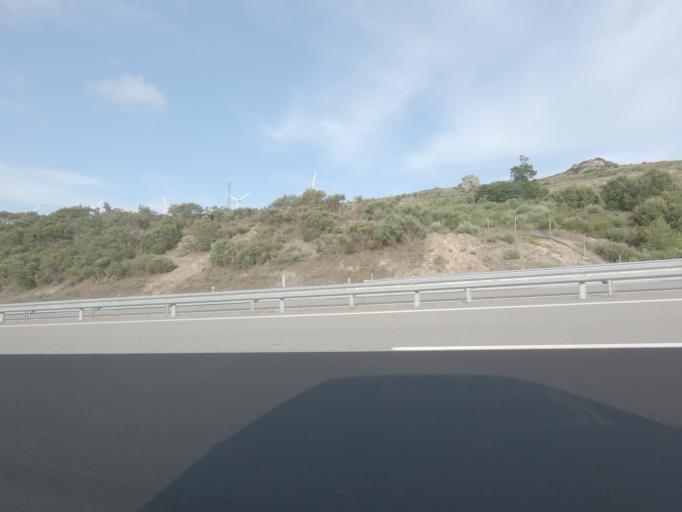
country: PT
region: Vila Real
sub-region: Vila Pouca de Aguiar
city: Vila Pouca de Aguiar
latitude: 41.4550
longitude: -7.6445
